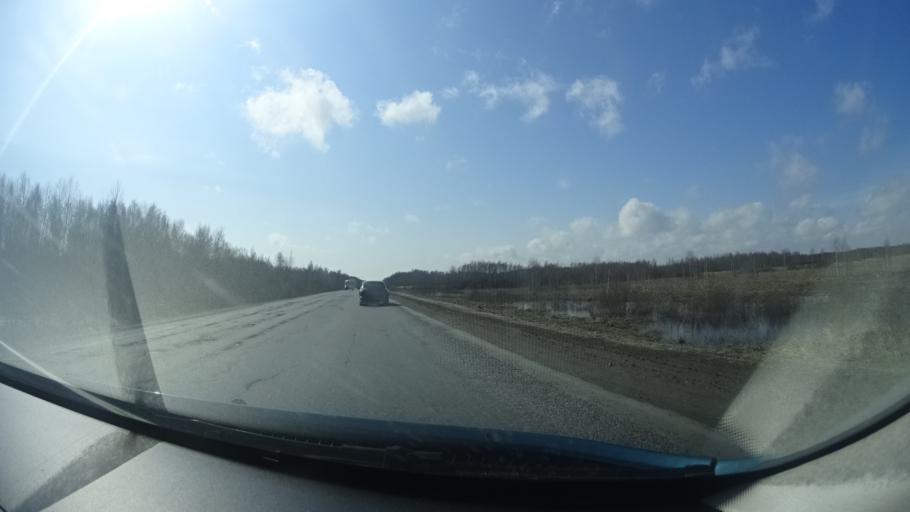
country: RU
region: Bashkortostan
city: Mikhaylovka
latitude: 54.9129
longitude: 55.7336
